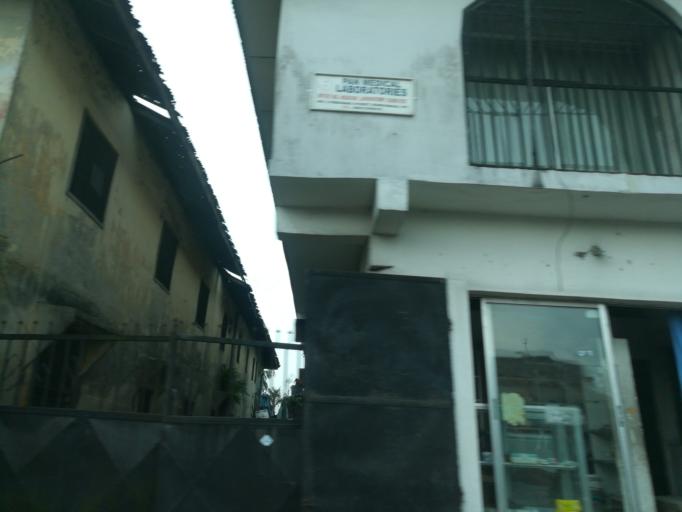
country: NG
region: Rivers
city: Port Harcourt
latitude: 4.8354
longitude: 7.0225
